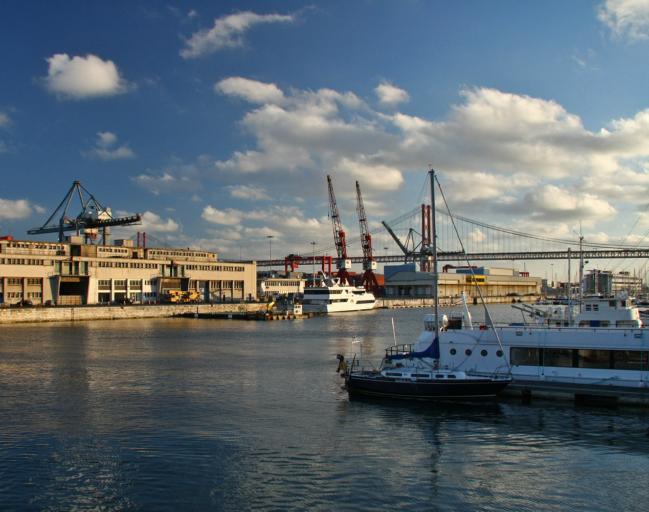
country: PT
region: Setubal
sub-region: Almada
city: Cacilhas
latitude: 38.7030
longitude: -9.1637
